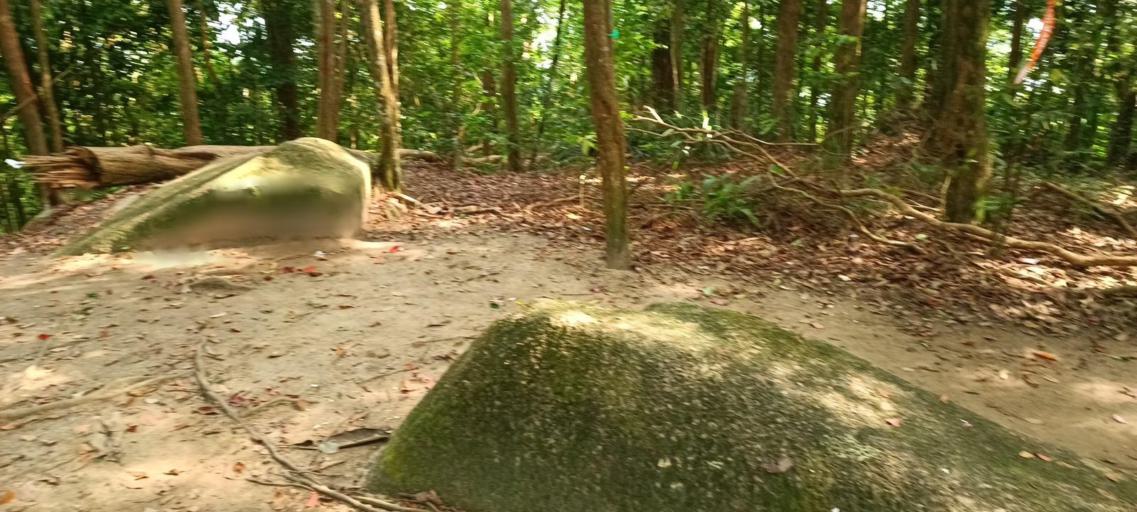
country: MY
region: Penang
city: Bukit Mertajam
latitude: 5.3721
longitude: 100.4847
